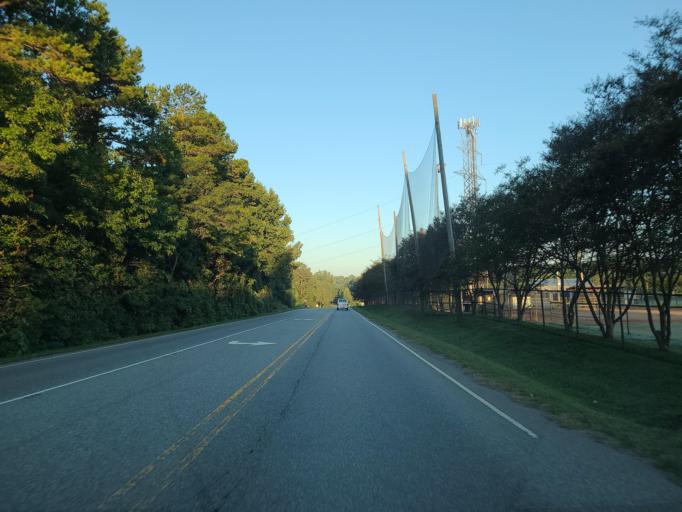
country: US
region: North Carolina
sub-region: Union County
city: Wesley Chapel
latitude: 35.0010
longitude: -80.7105
